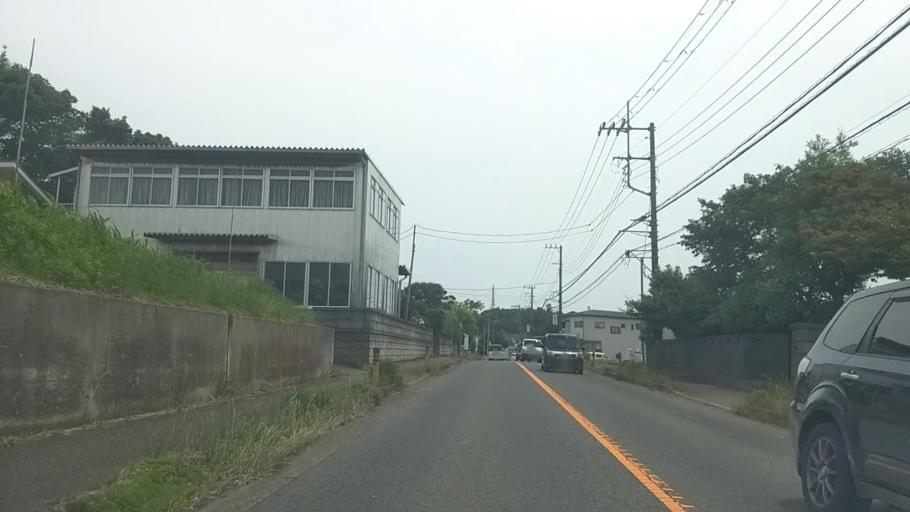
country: JP
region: Kanagawa
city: Chigasaki
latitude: 35.3641
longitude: 139.4218
